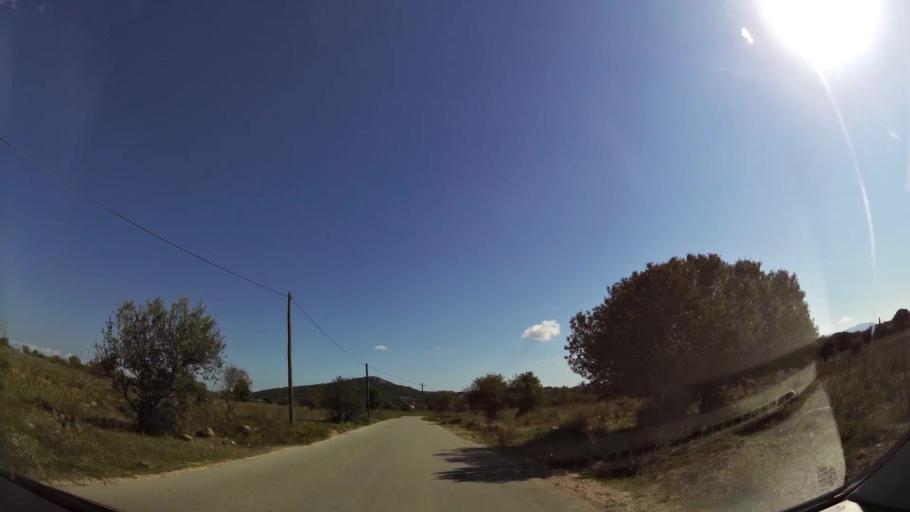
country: GR
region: Attica
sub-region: Nomarchia Anatolikis Attikis
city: Pikermi
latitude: 38.0092
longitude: 23.9413
